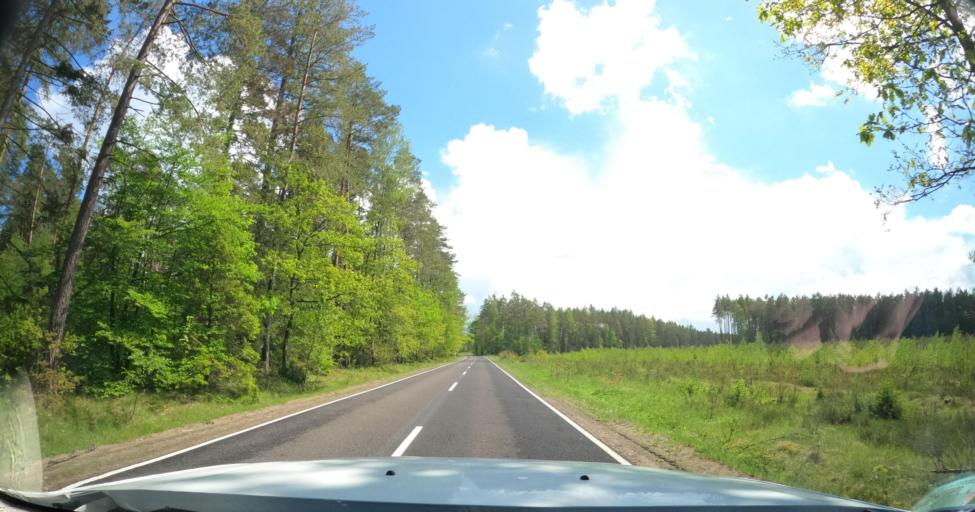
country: PL
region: Pomeranian Voivodeship
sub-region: Powiat slupski
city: Potegowo
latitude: 54.3923
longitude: 17.4729
